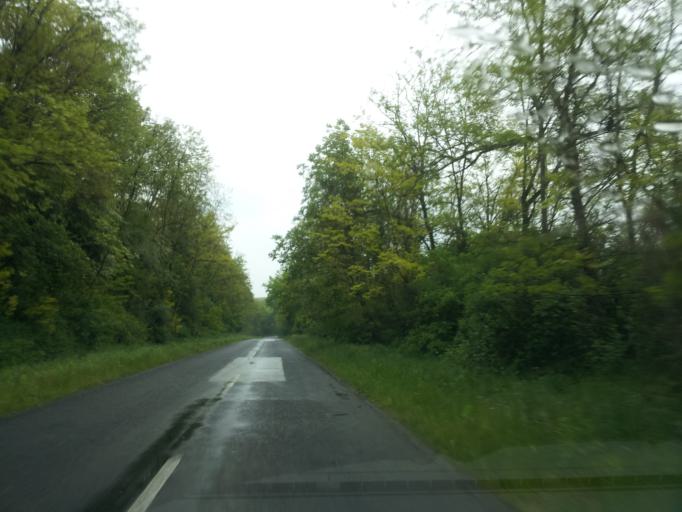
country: HU
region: Tolna
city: Bonyhad
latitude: 46.2605
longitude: 18.6087
